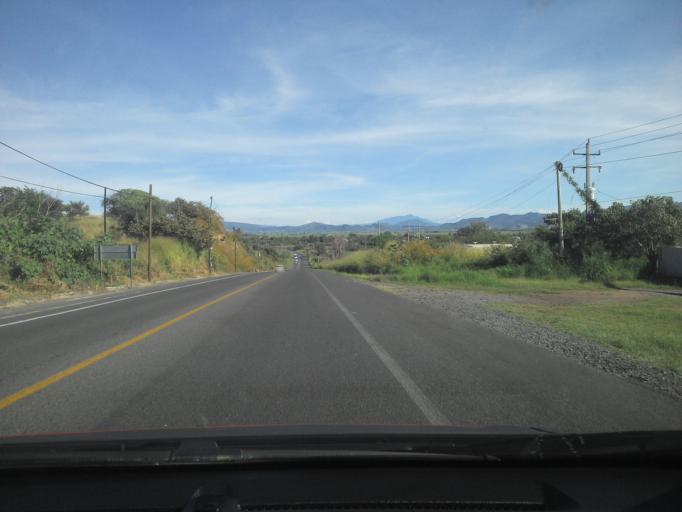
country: MX
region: Jalisco
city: Teuchitlan
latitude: 20.6777
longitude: -103.8371
